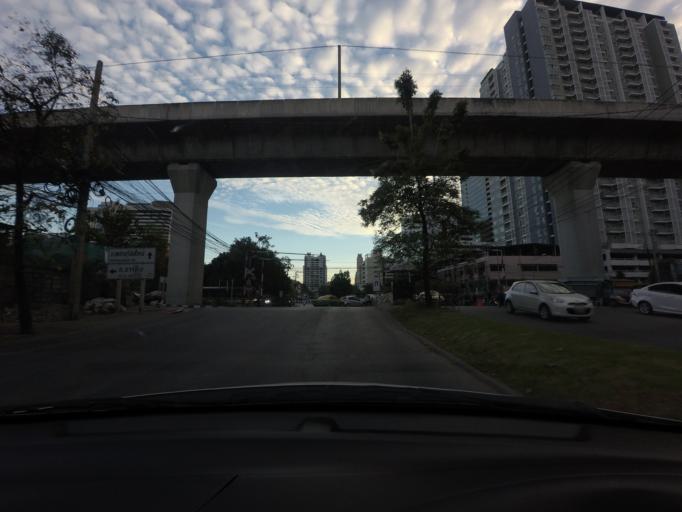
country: TH
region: Bangkok
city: Watthana
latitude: 13.7494
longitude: 100.5687
